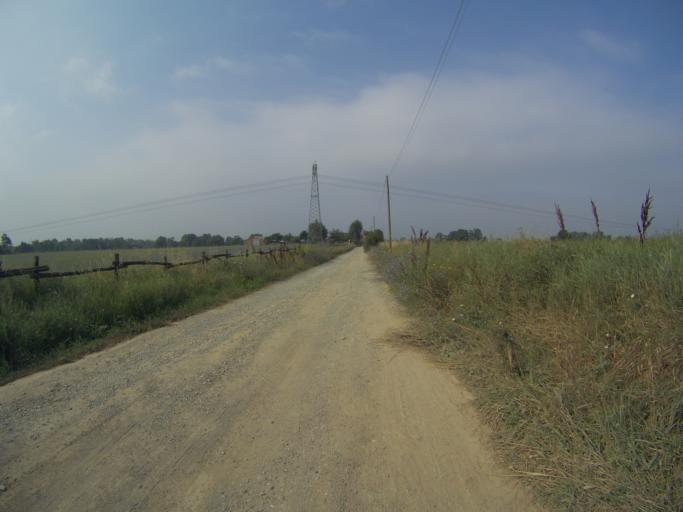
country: IT
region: Emilia-Romagna
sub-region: Provincia di Reggio Emilia
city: Albinea
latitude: 44.6413
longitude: 10.6197
